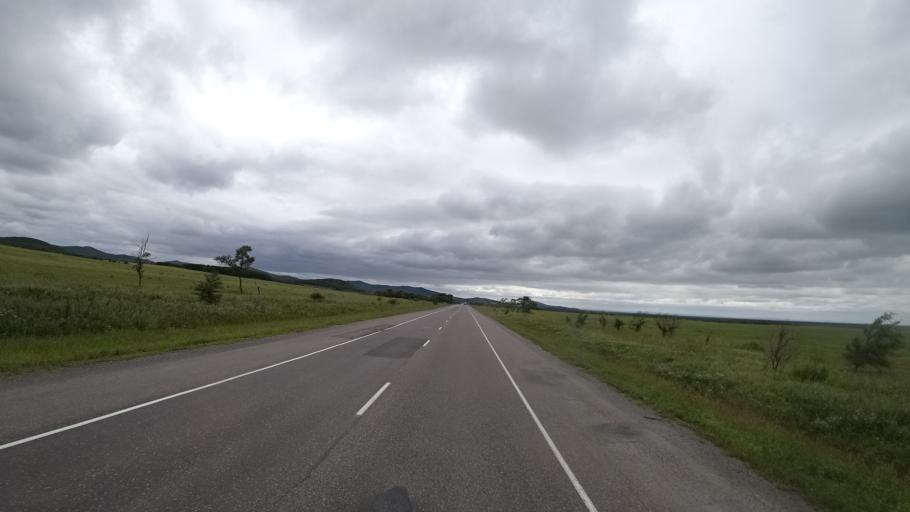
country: RU
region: Primorskiy
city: Chernigovka
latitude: 44.3022
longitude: 132.5309
